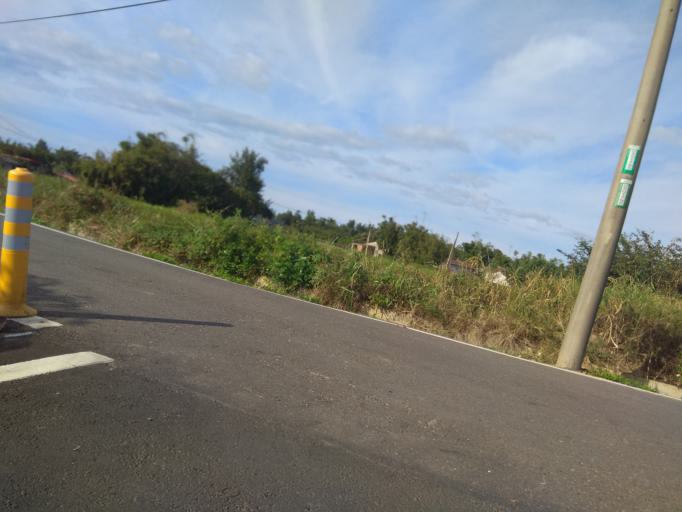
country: TW
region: Taiwan
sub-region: Hsinchu
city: Zhubei
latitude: 24.9564
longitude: 121.0049
